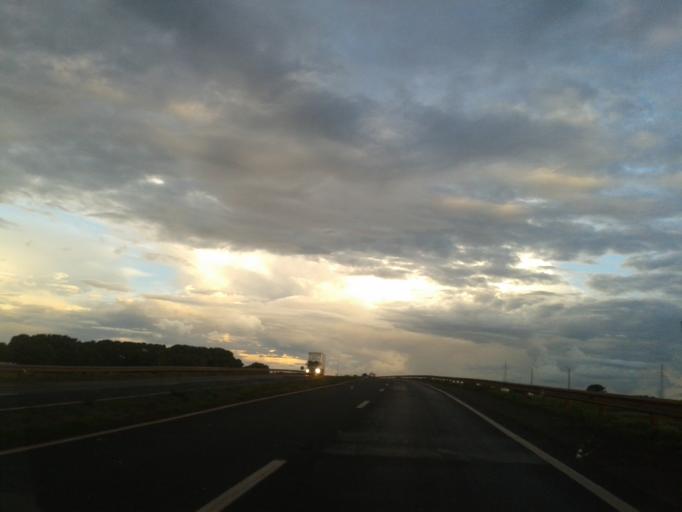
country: BR
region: Minas Gerais
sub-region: Centralina
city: Centralina
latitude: -18.7090
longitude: -49.1390
